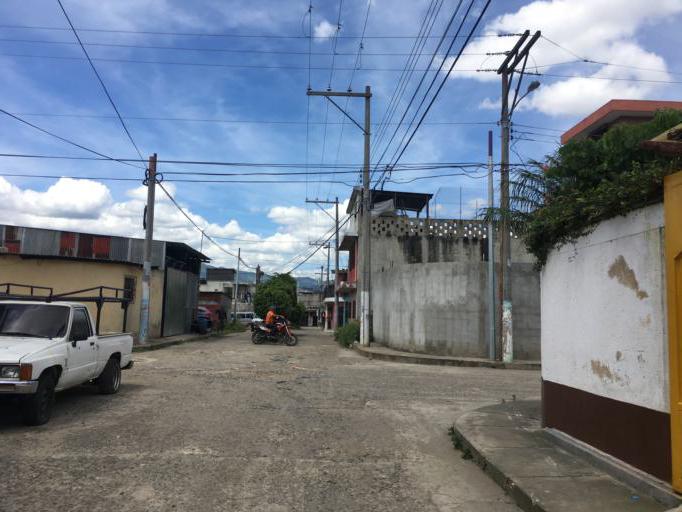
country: GT
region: Guatemala
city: Petapa
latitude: 14.5006
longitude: -90.5694
